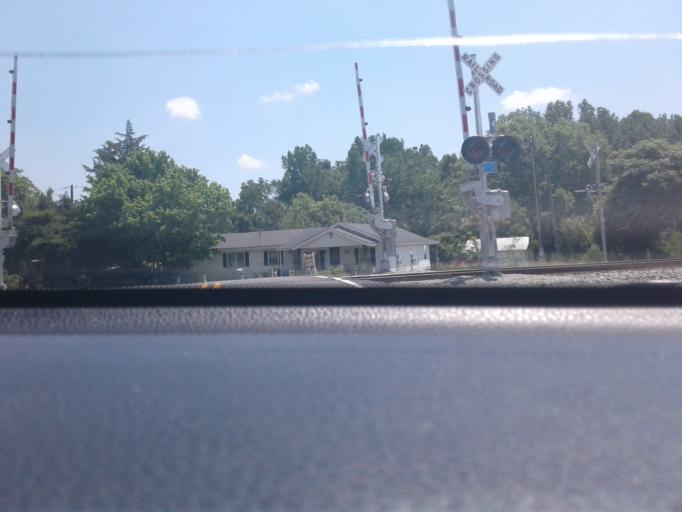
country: US
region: North Carolina
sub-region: Harnett County
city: Dunn
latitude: 35.3426
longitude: -78.5813
